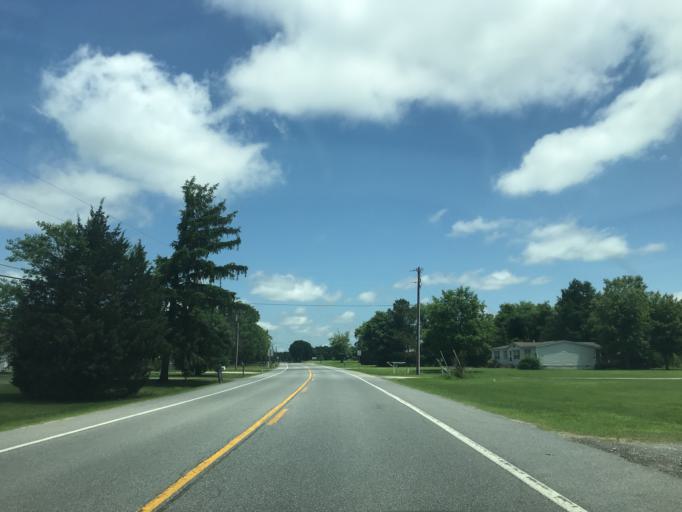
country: US
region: Maryland
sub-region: Caroline County
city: Federalsburg
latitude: 38.7029
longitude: -75.7548
